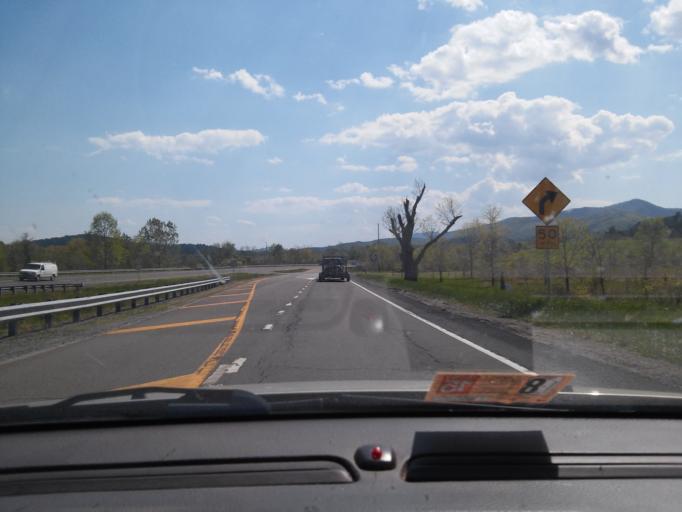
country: US
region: Virginia
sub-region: Rappahannock County
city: Washington
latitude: 38.6634
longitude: -78.2182
